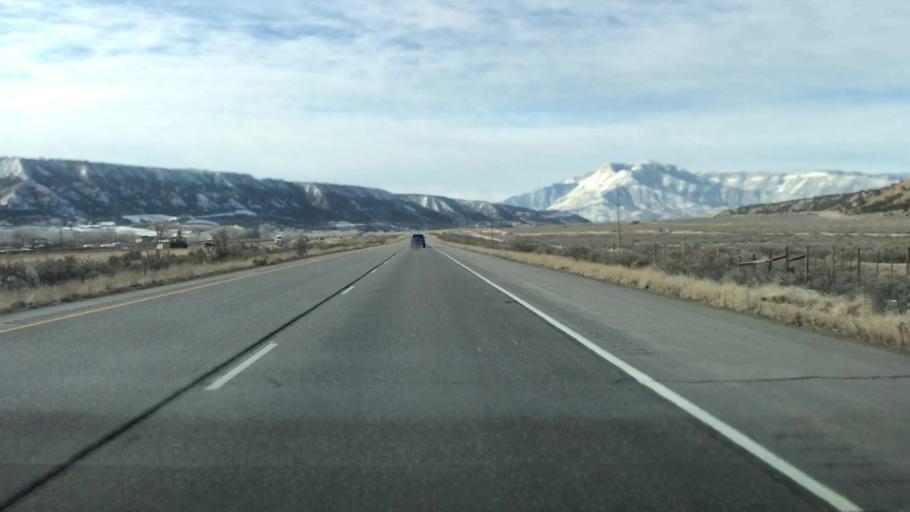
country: US
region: Colorado
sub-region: Garfield County
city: Battlement Mesa
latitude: 39.4852
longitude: -107.9630
